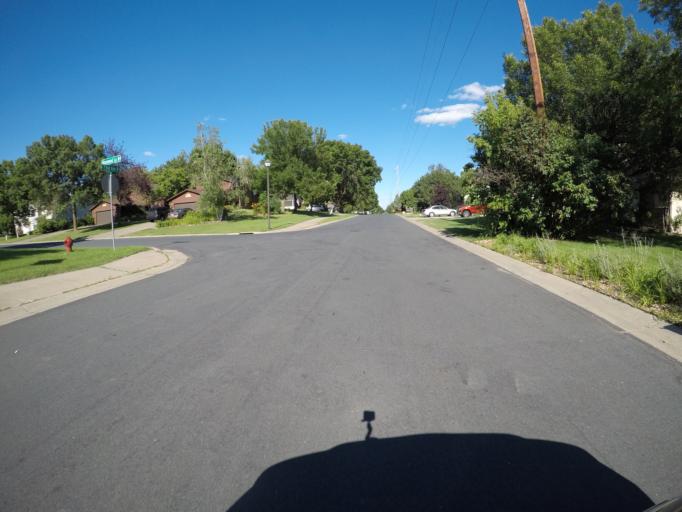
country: US
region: Minnesota
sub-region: Hennepin County
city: Maple Grove
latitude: 45.0874
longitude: -93.4448
